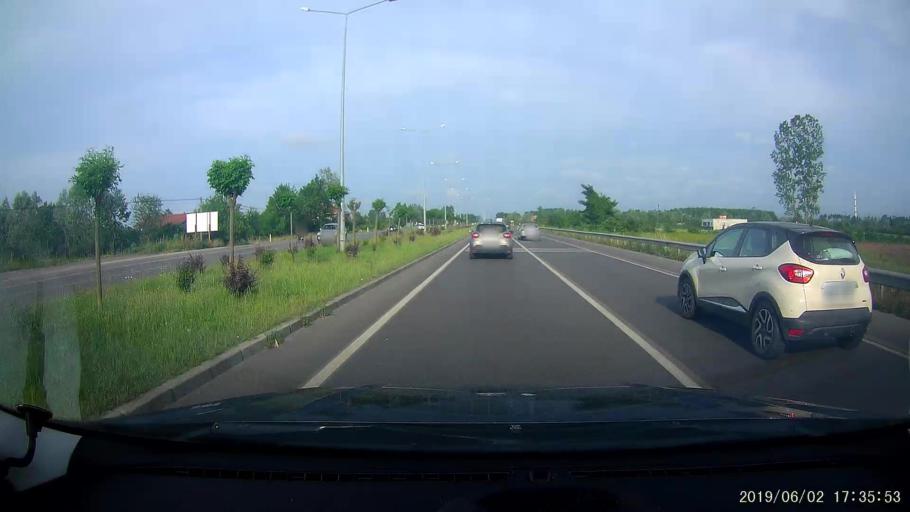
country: TR
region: Samsun
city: Terme
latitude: 41.2193
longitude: 36.8893
